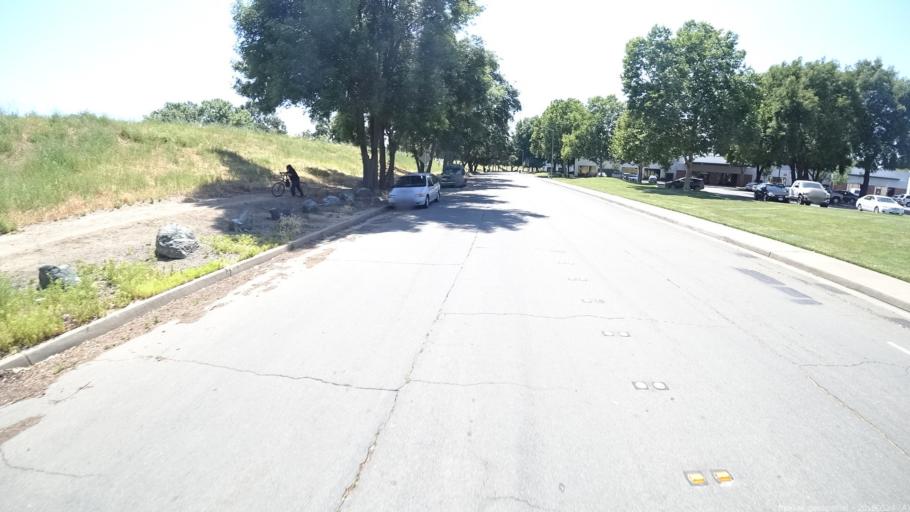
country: US
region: California
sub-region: Sacramento County
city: Sacramento
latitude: 38.5955
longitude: -121.4595
